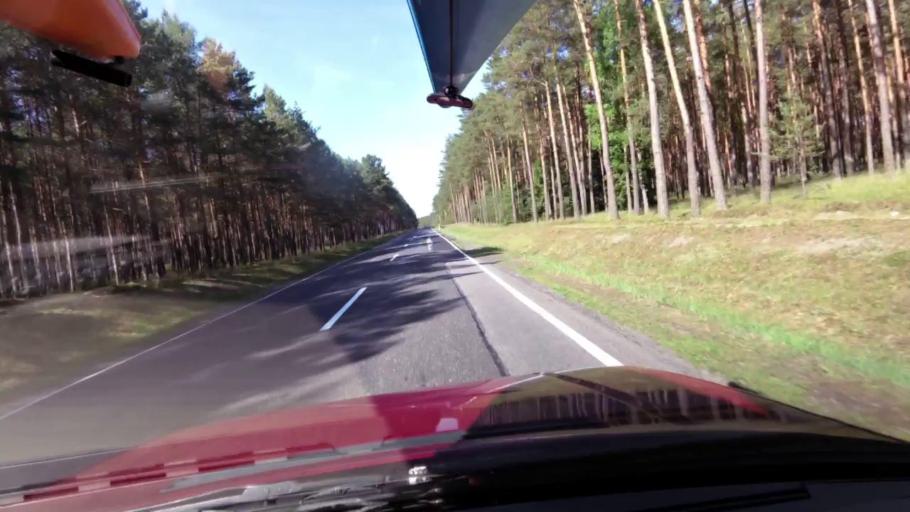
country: PL
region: Pomeranian Voivodeship
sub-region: Powiat bytowski
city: Trzebielino
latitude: 54.1669
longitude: 17.0598
